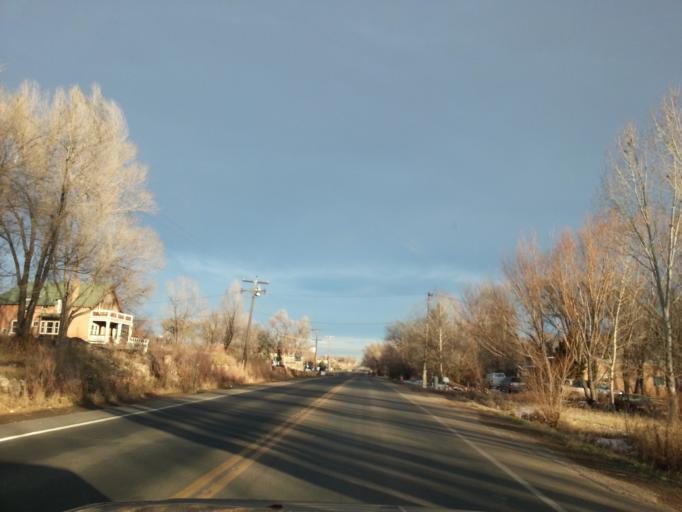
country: US
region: Colorado
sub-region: Larimer County
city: Loveland
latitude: 40.4073
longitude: -105.1369
